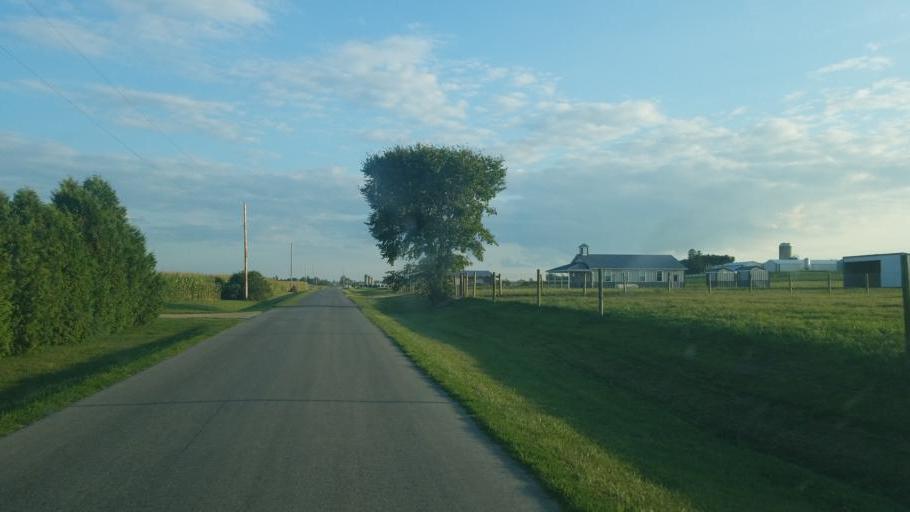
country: US
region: Ohio
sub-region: Huron County
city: Greenwich
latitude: 41.0177
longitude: -82.5596
